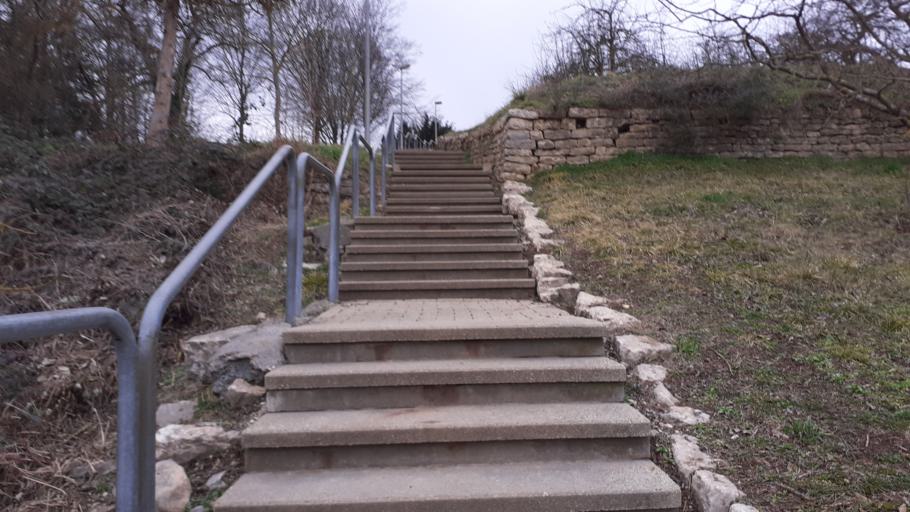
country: DE
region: Baden-Wuerttemberg
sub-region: Regierungsbezirk Stuttgart
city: Mundelsheim
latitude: 48.9954
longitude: 9.2118
